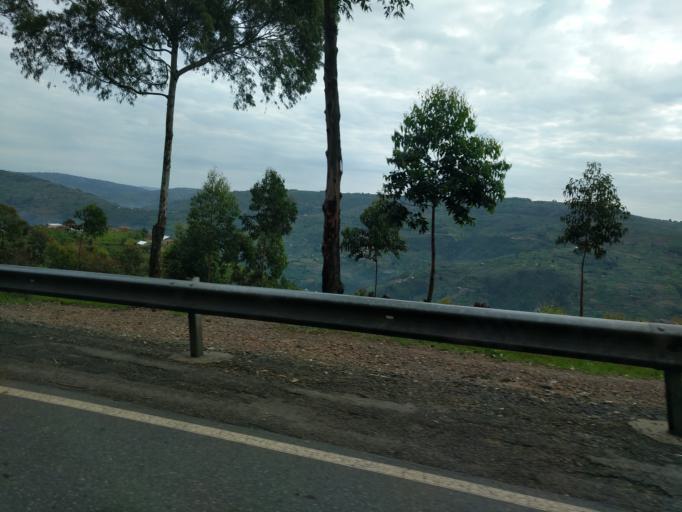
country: RW
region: Kigali
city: Kigali
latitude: -1.7908
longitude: 29.9305
